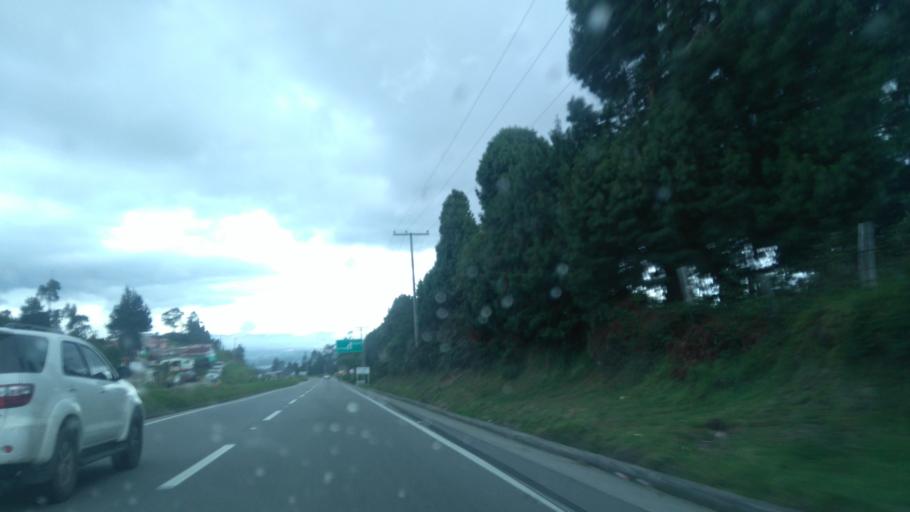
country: CO
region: Cundinamarca
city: El Rosal
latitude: 4.8697
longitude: -74.2899
